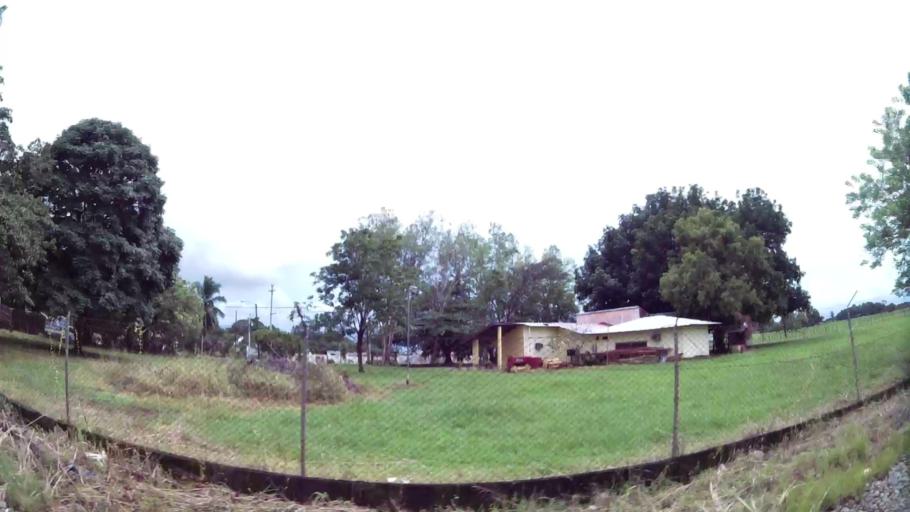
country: PA
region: Chiriqui
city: David
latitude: 8.4142
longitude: -82.4536
